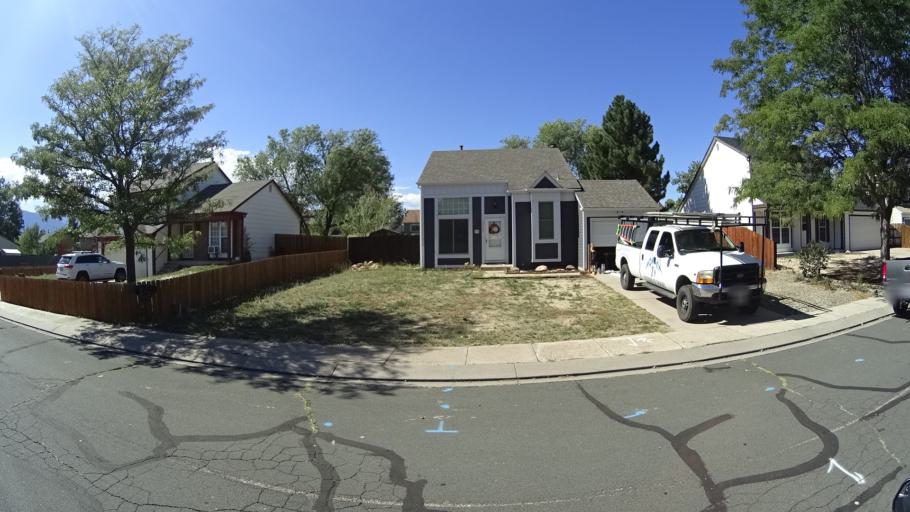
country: US
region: Colorado
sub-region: El Paso County
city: Stratmoor
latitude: 38.7931
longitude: -104.7367
